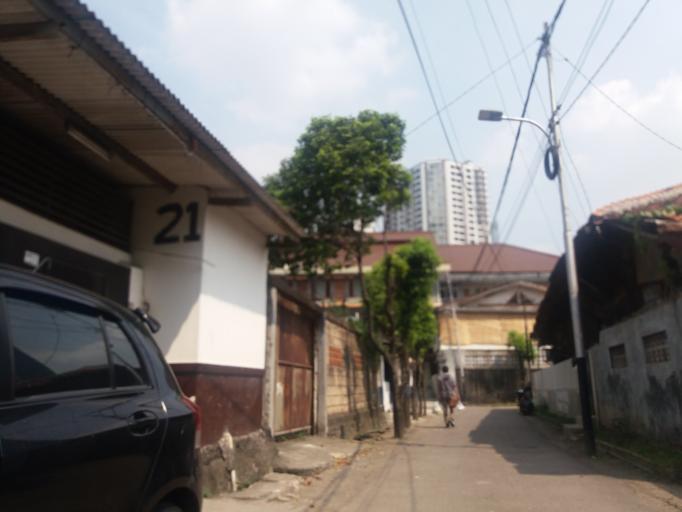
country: ID
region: Jakarta Raya
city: Jakarta
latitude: -6.2235
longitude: 106.8192
